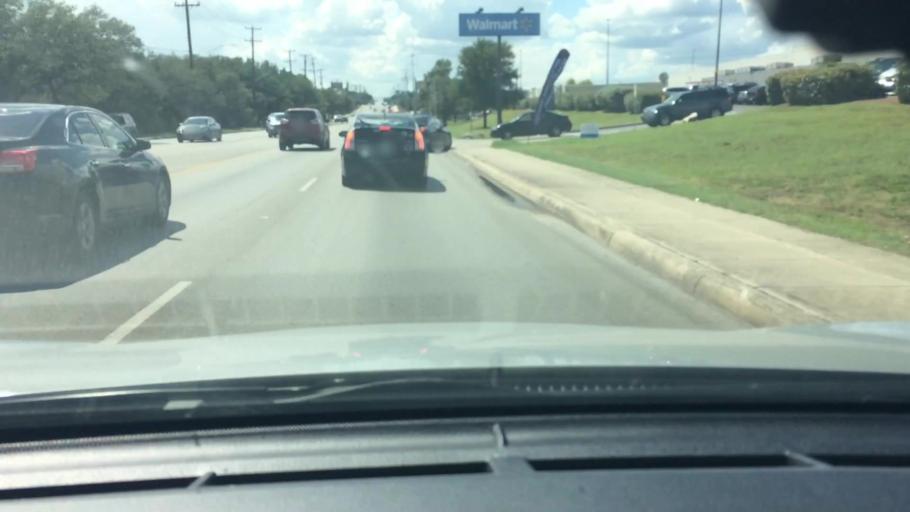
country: US
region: Texas
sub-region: Bexar County
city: Shavano Park
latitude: 29.5632
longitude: -98.5949
